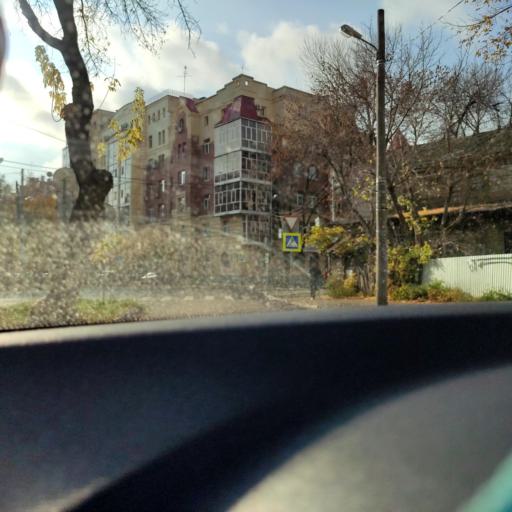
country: RU
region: Samara
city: Samara
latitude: 53.1980
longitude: 50.1143
